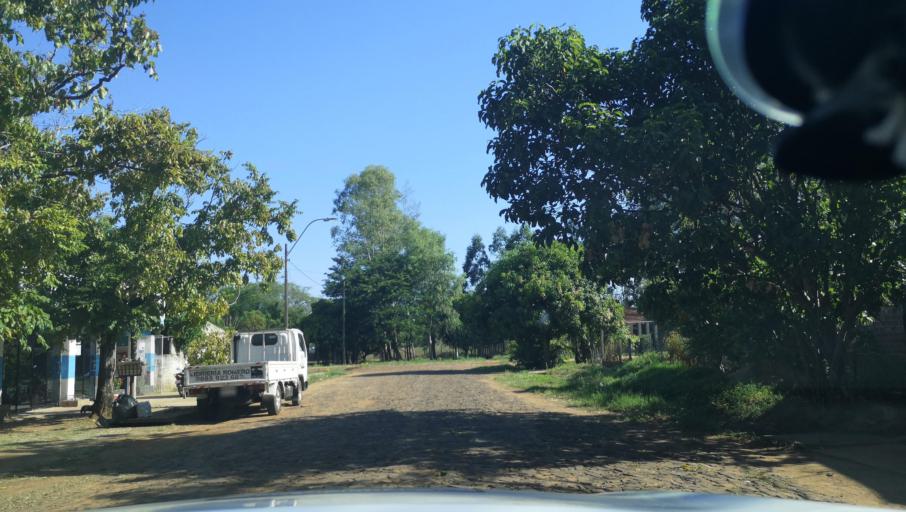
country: PY
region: Itapua
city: Carmen del Parana
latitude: -27.1541
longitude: -56.2384
